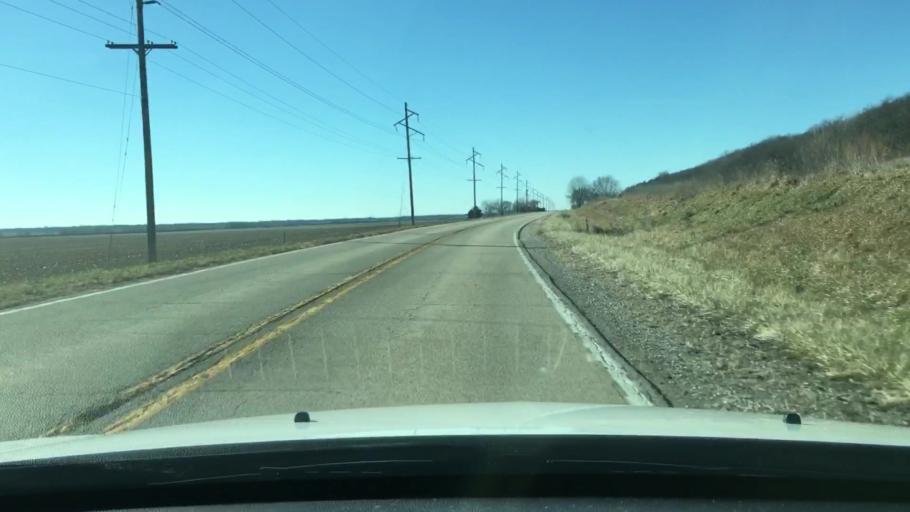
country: US
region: Illinois
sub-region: Fulton County
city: Astoria
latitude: 40.1855
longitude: -90.2134
